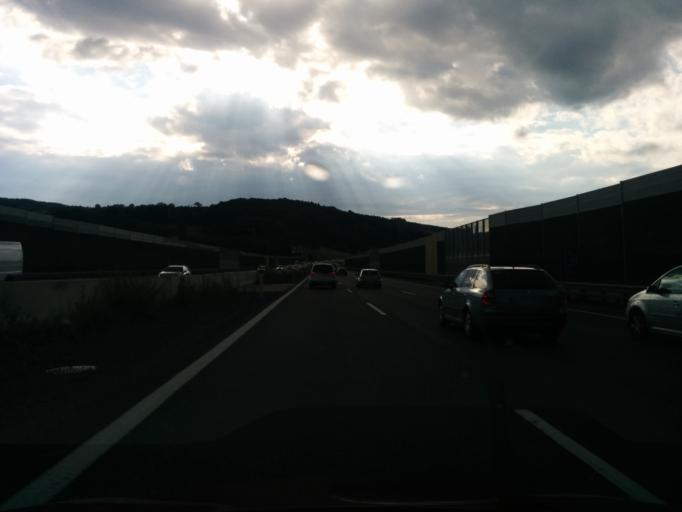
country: AT
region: Lower Austria
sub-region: Politischer Bezirk Sankt Polten
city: Altlengbach
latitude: 48.1539
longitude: 15.9090
